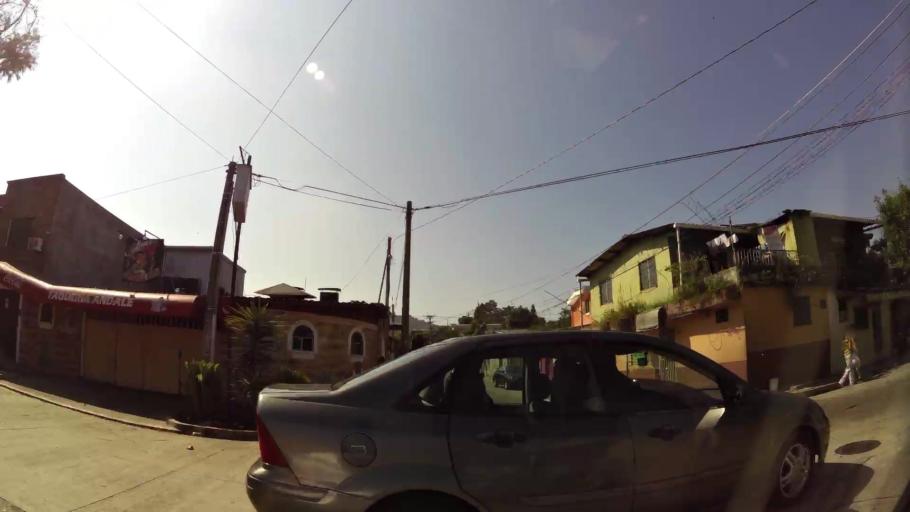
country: SV
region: La Libertad
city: Antiguo Cuscatlan
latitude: 13.6728
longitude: -89.2396
